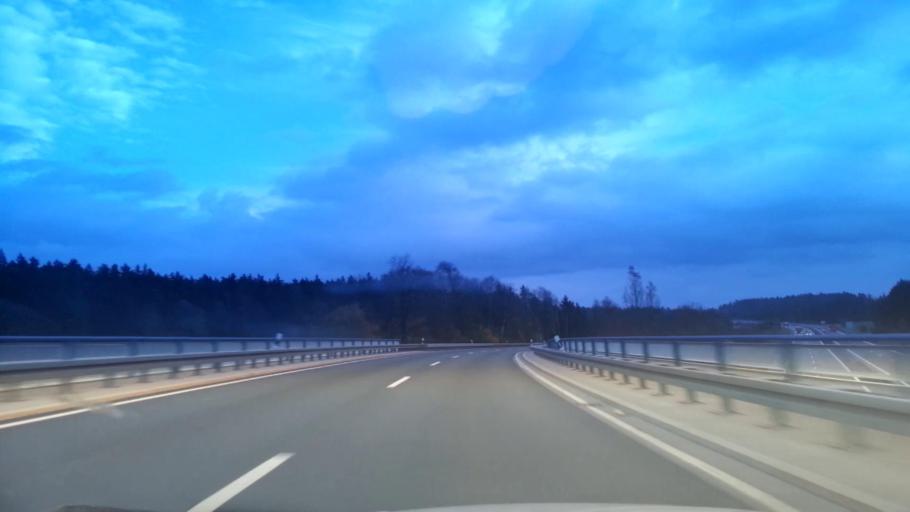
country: DE
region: Bavaria
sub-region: Upper Palatinate
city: Pechbrunn
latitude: 49.9707
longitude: 12.1788
